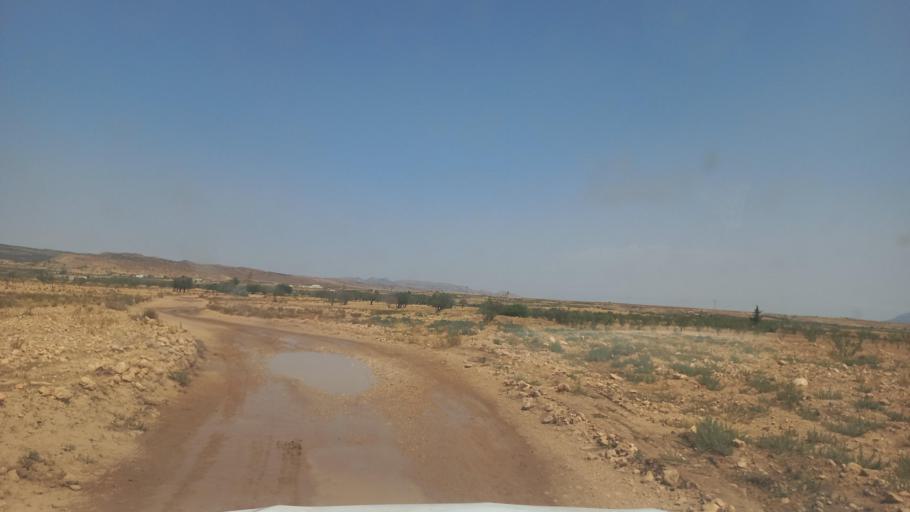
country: TN
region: Al Qasrayn
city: Kasserine
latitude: 35.2851
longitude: 8.9505
